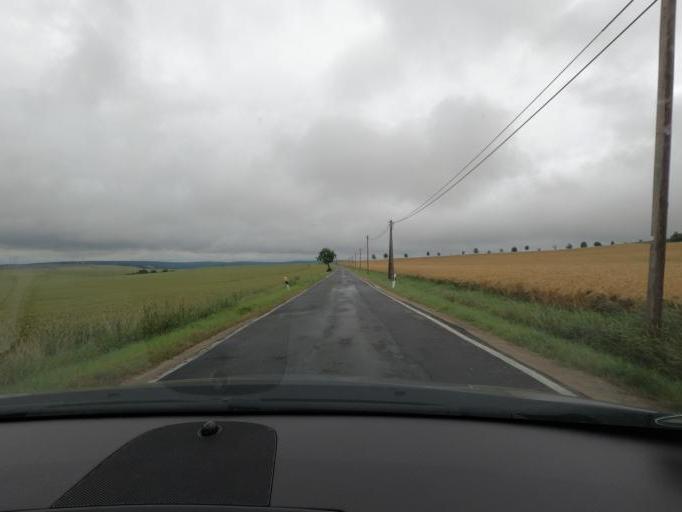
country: DE
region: Thuringia
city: Geisleden
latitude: 51.3243
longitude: 10.1979
